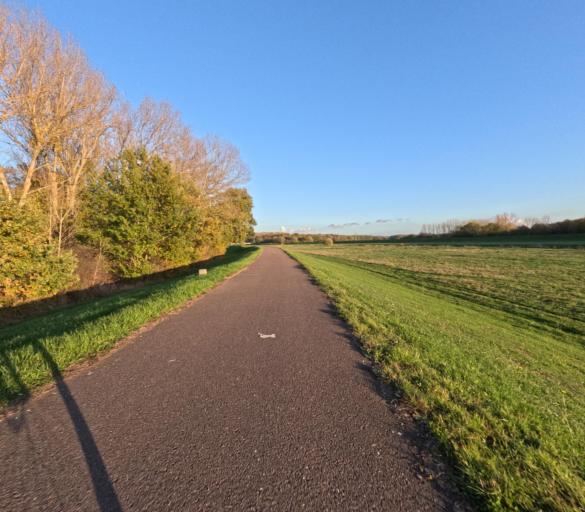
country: DE
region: Saxony-Anhalt
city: Ermlitz
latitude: 51.3841
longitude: 12.1401
